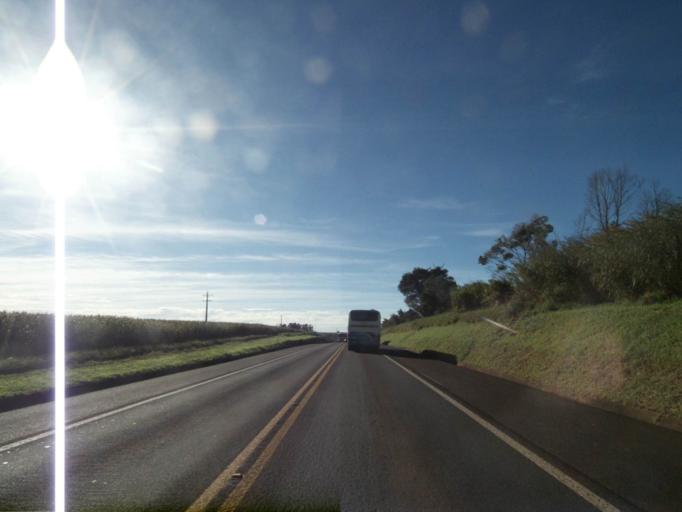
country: BR
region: Parana
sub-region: Cascavel
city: Cascavel
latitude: -25.0285
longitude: -53.5646
